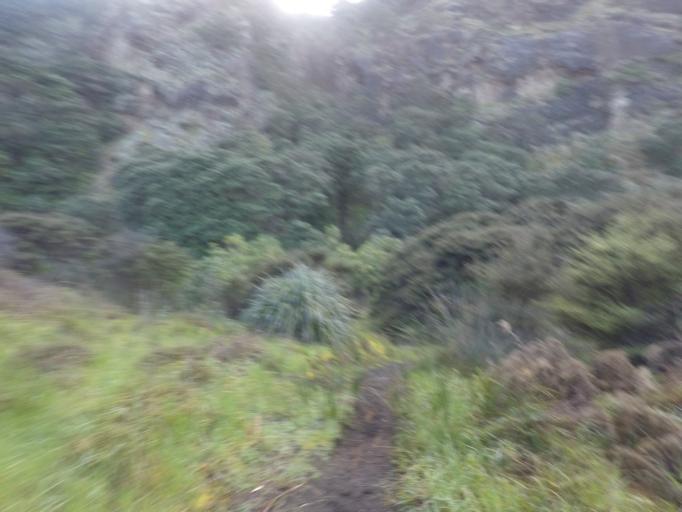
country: NZ
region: Auckland
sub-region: Auckland
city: Muriwai Beach
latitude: -37.0001
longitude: 174.4793
